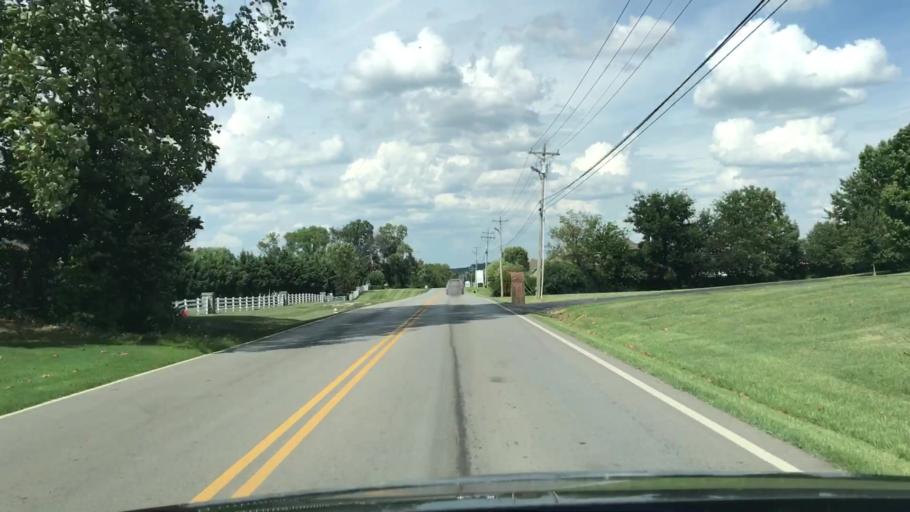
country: US
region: Tennessee
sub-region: Maury County
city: Spring Hill
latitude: 35.7576
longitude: -86.8829
